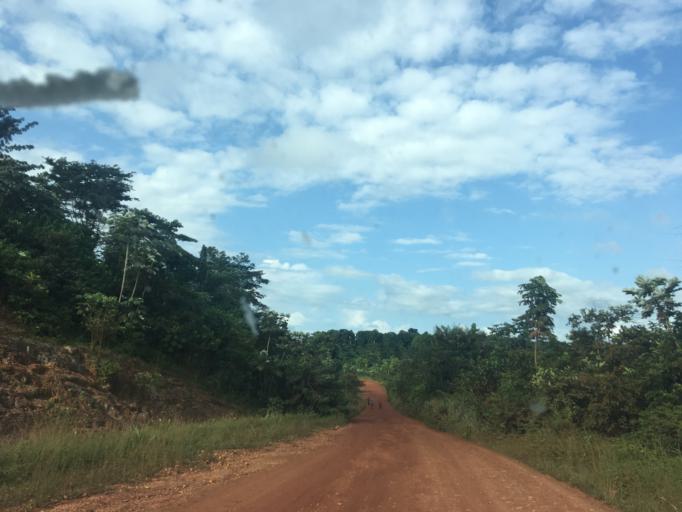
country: GH
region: Western
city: Wassa-Akropong
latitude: 5.9540
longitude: -2.4365
